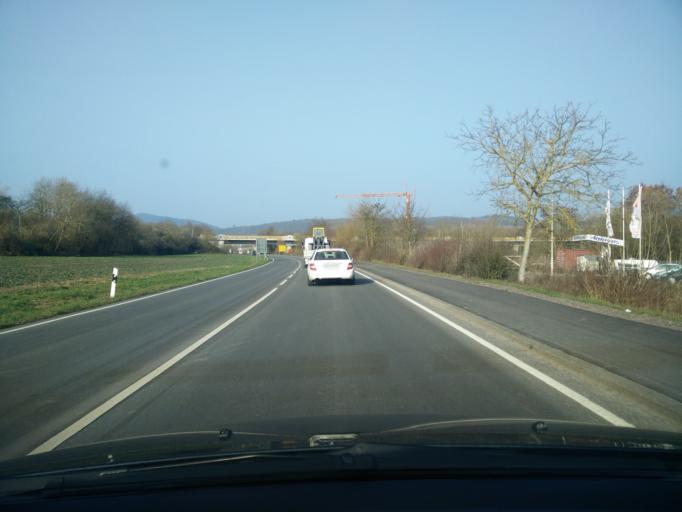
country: DE
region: Rheinland-Pfalz
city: Kapellen-Drusweiler
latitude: 49.1026
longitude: 8.0192
